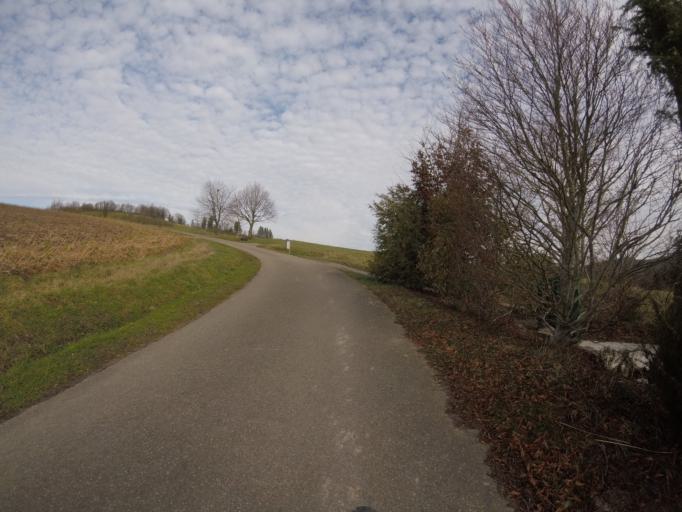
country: DE
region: Baden-Wuerttemberg
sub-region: Regierungsbezirk Stuttgart
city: Oppenweiler
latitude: 48.9952
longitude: 9.4651
